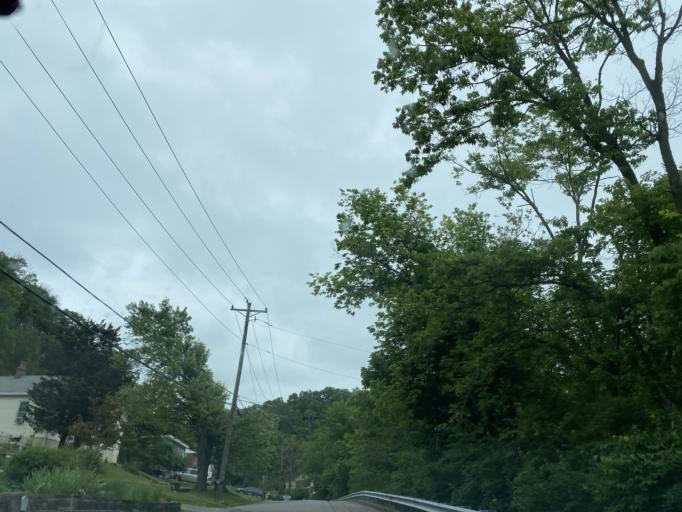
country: US
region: Kentucky
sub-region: Campbell County
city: Bellevue
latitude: 39.0999
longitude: -84.4664
